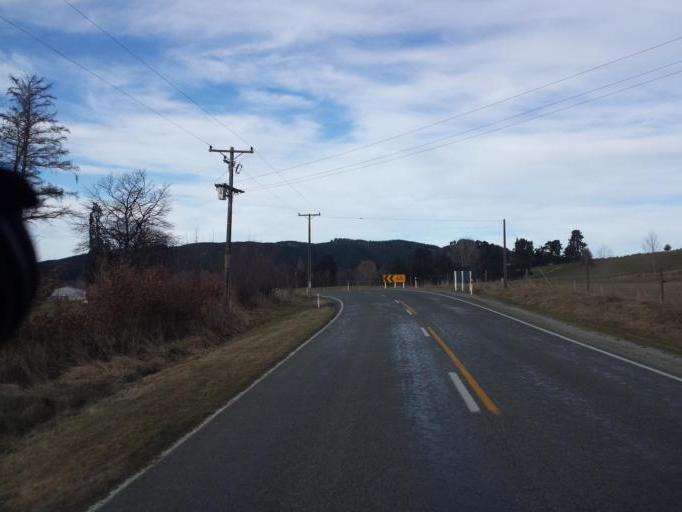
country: NZ
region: Canterbury
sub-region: Timaru District
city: Pleasant Point
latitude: -44.1188
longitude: 171.0249
